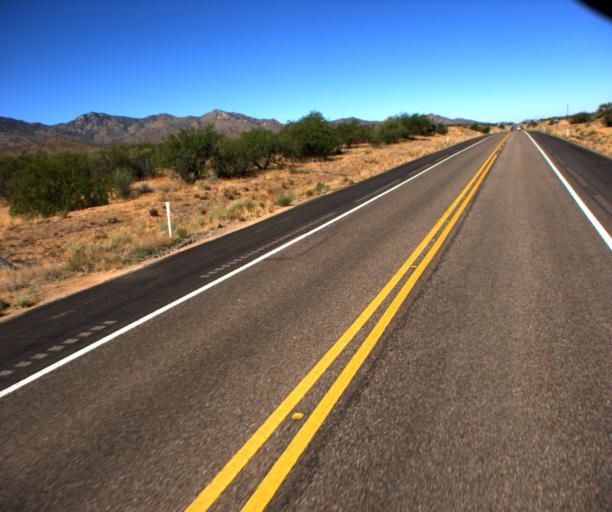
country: US
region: Arizona
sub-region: Pima County
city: Three Points
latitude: 32.0264
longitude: -111.5798
